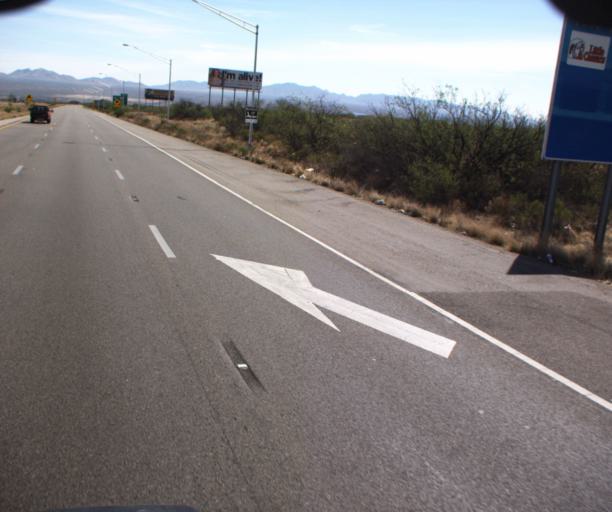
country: US
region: Arizona
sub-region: Cochise County
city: Whetstone
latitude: 31.9658
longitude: -110.3411
